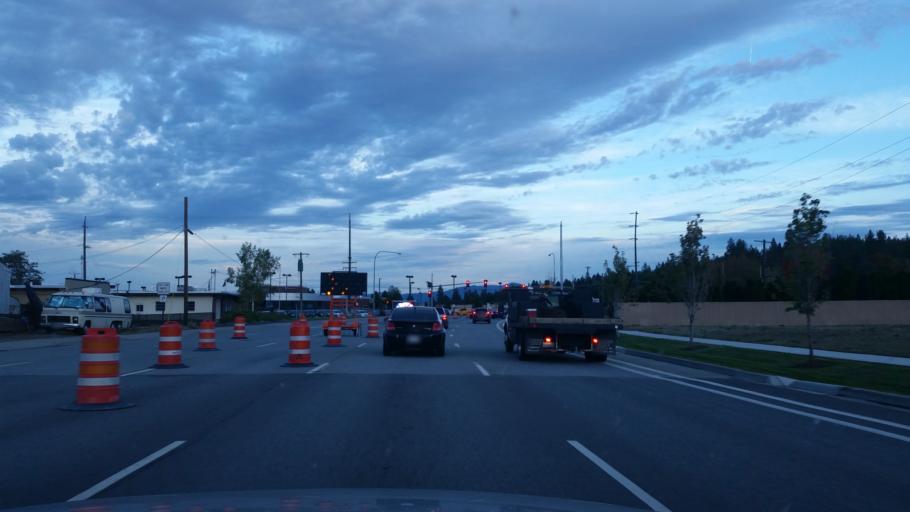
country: US
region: Washington
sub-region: Spokane County
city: Dishman
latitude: 47.6559
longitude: -117.3060
